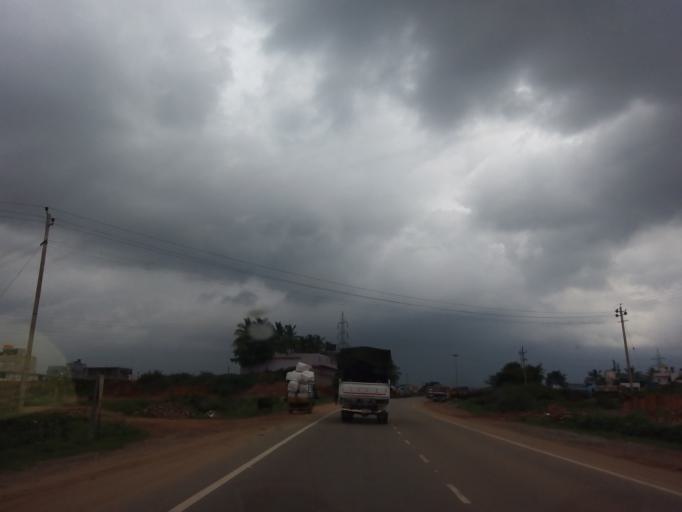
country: IN
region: Karnataka
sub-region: Hassan
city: Hassan
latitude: 12.9887
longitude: 76.1103
